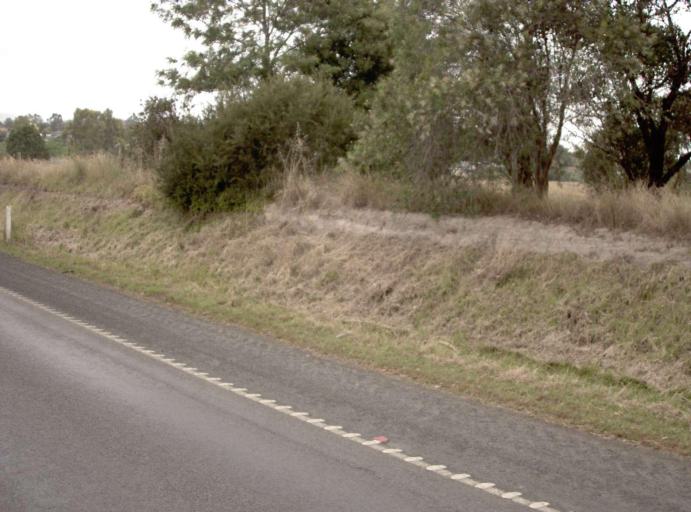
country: AU
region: Victoria
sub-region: Latrobe
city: Morwell
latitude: -38.2983
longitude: 146.4178
